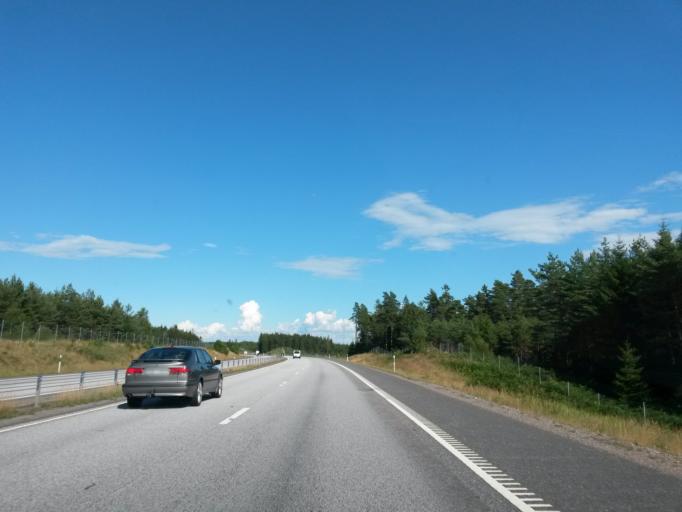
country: SE
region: Vaestra Goetaland
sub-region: Uddevalla Kommun
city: Uddevalla
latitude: 58.3282
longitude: 12.0350
